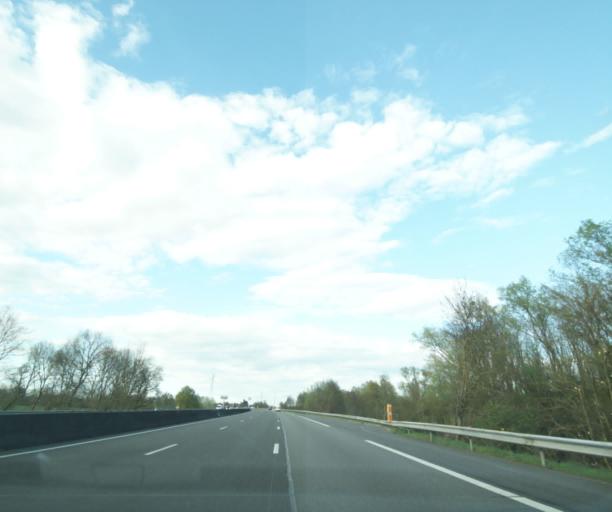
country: FR
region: Rhone-Alpes
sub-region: Departement du Rhone
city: Belleville
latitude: 46.1089
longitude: 4.7590
